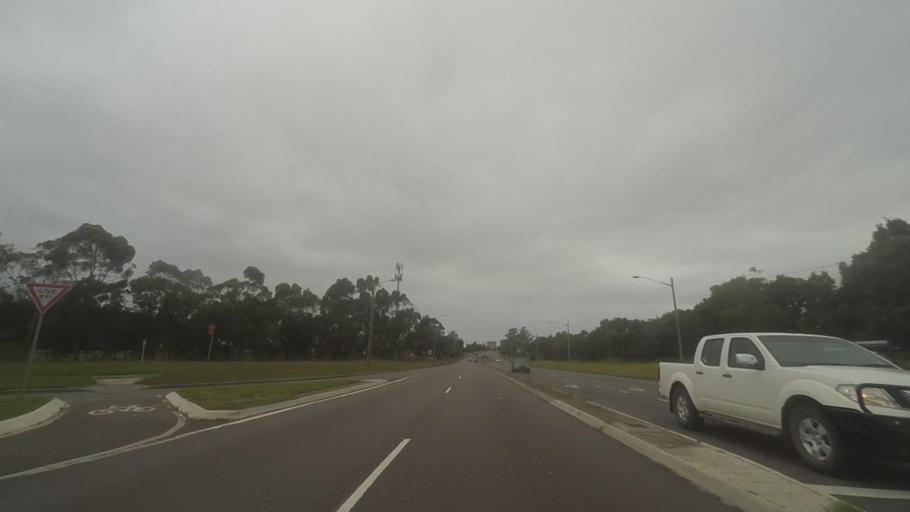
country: AU
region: New South Wales
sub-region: Newcastle
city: Mayfield West
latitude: -32.8871
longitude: 151.7322
